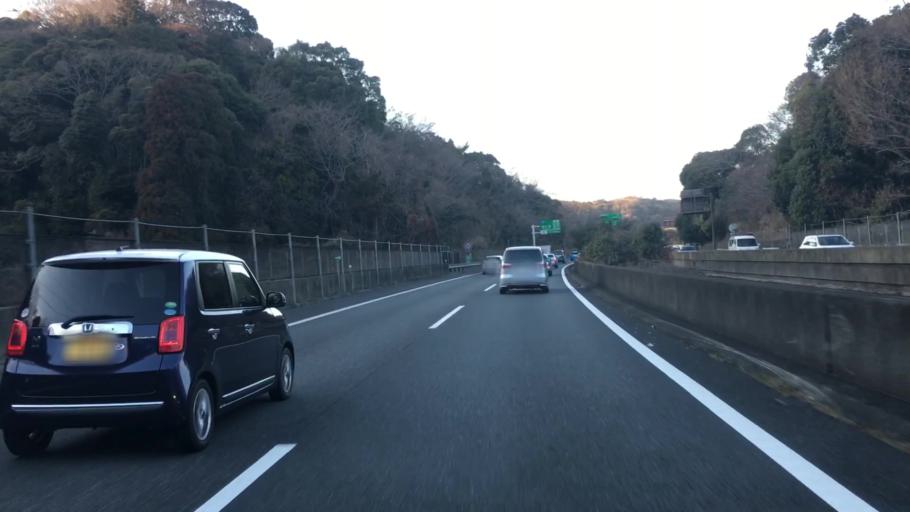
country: JP
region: Kanagawa
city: Zushi
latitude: 35.3281
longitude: 139.5949
